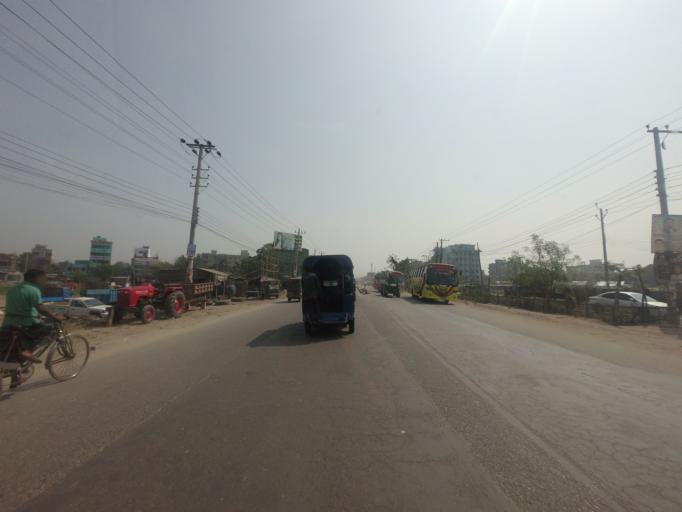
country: BD
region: Dhaka
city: Bhairab Bazar
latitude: 24.0556
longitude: 90.9784
